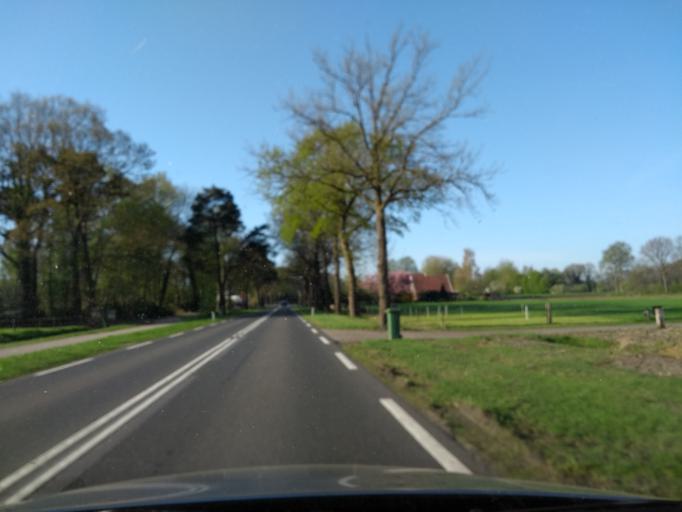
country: NL
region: Overijssel
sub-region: Gemeente Hof van Twente
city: Hengevelde
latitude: 52.2152
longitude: 6.6675
